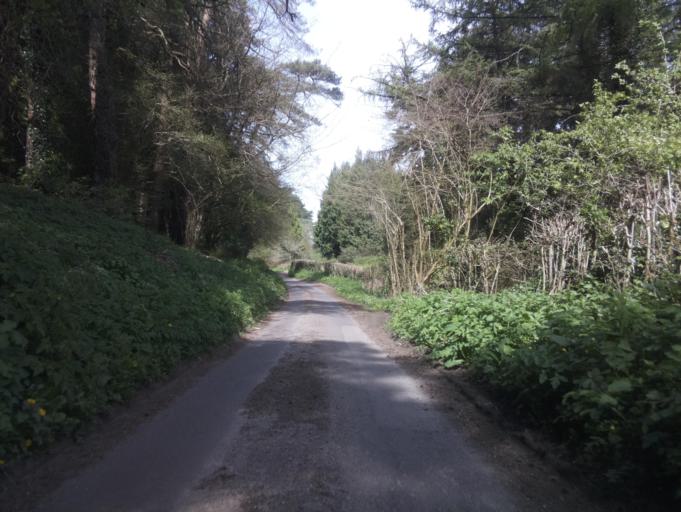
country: GB
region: England
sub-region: Dorset
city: Sherborne
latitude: 50.9712
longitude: -2.5321
